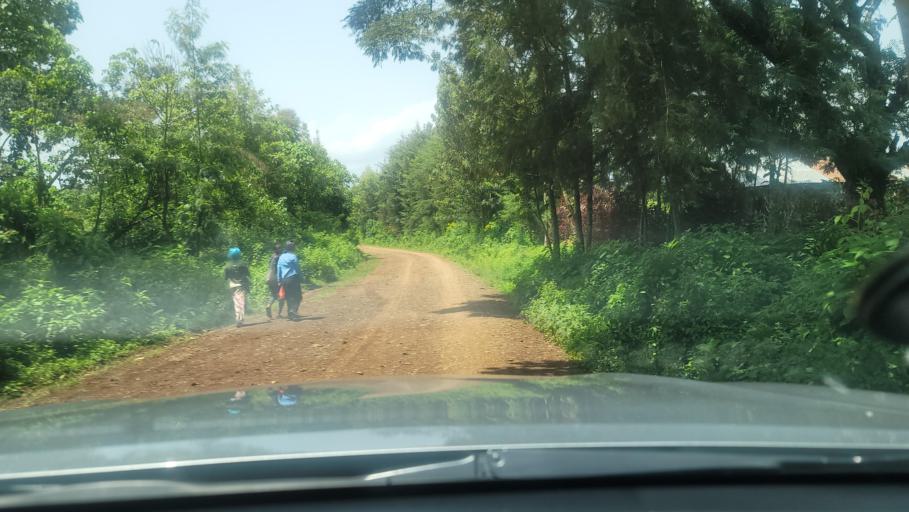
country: ET
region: Oromiya
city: Agaro
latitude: 7.8067
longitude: 36.4138
